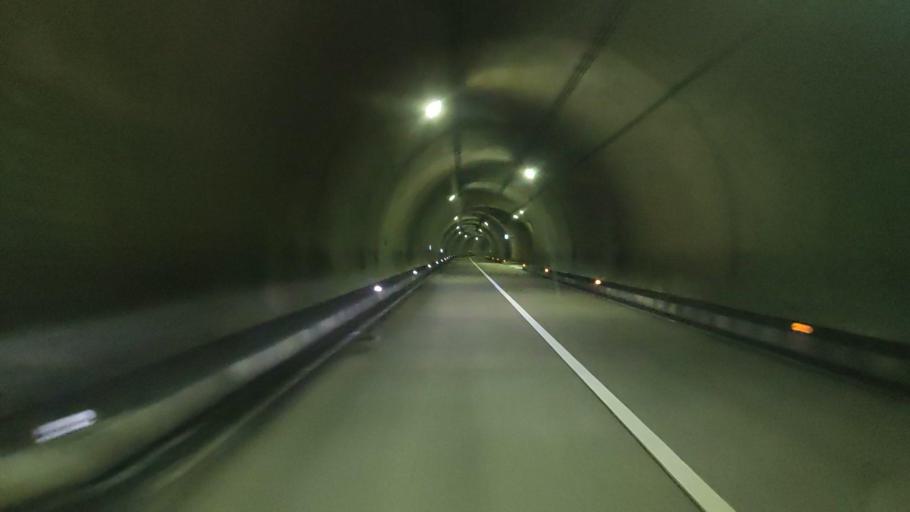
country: JP
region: Wakayama
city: Shingu
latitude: 33.8559
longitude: 135.8528
